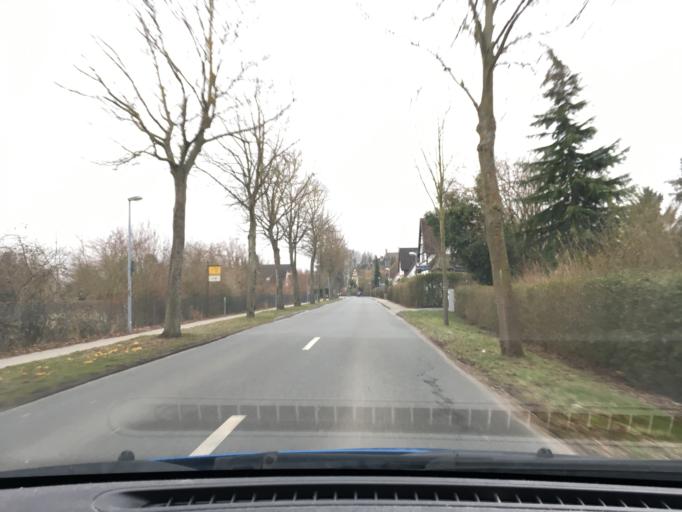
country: DE
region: Lower Saxony
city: Lueneburg
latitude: 53.2587
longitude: 10.3855
